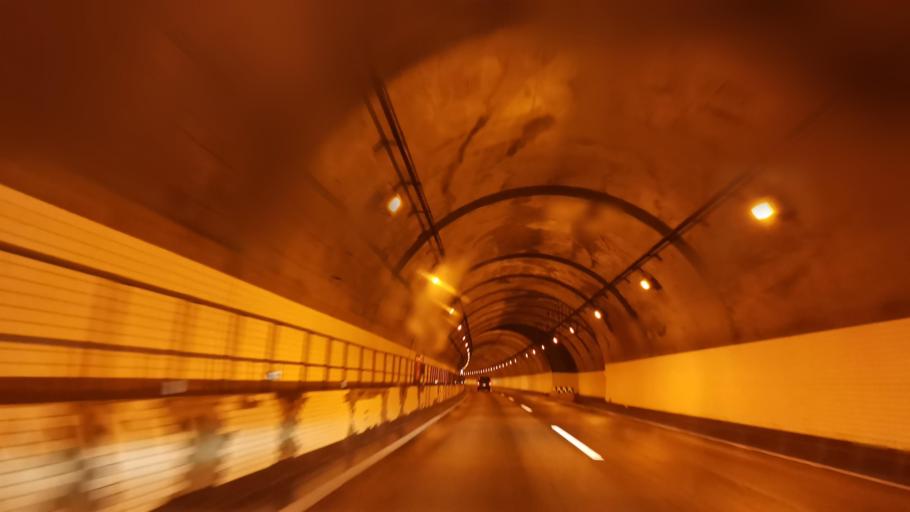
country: JP
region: Hokkaido
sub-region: Asahikawa-shi
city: Asahikawa
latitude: 43.7920
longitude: 142.2571
